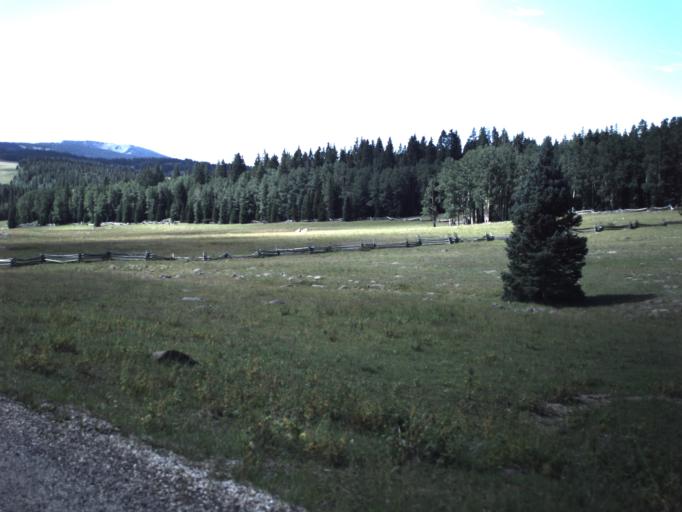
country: US
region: Utah
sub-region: Piute County
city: Junction
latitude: 38.2962
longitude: -112.3597
